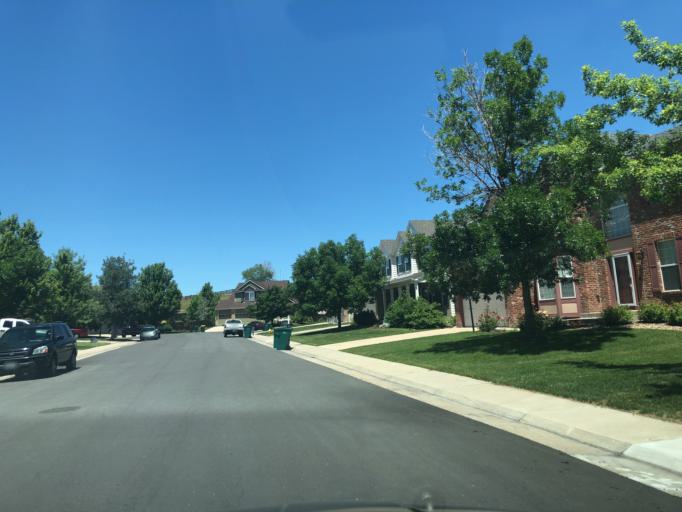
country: US
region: Colorado
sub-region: Arapahoe County
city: Dove Valley
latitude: 39.6117
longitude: -104.7574
